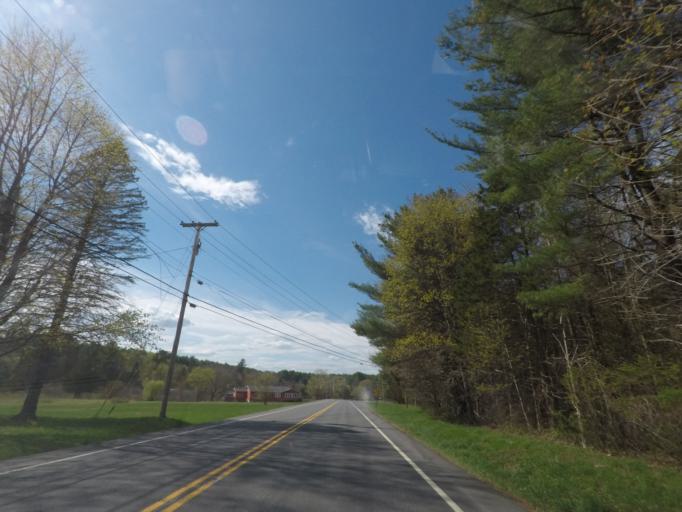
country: US
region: New York
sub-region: Greene County
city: Cairo
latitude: 42.3143
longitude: -74.0105
